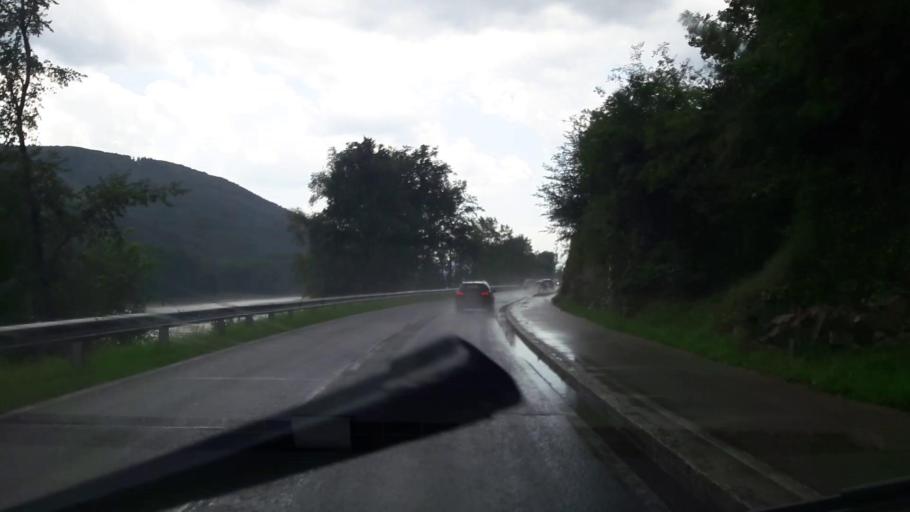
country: AT
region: Lower Austria
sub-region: Politischer Bezirk Krems
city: Aggsbach
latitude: 48.2831
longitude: 15.3972
